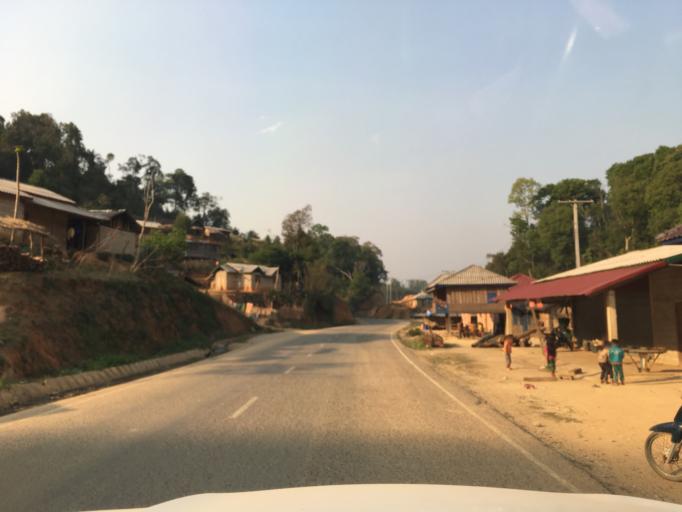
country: LA
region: Houaphan
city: Xam Nua
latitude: 20.5961
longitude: 104.0680
